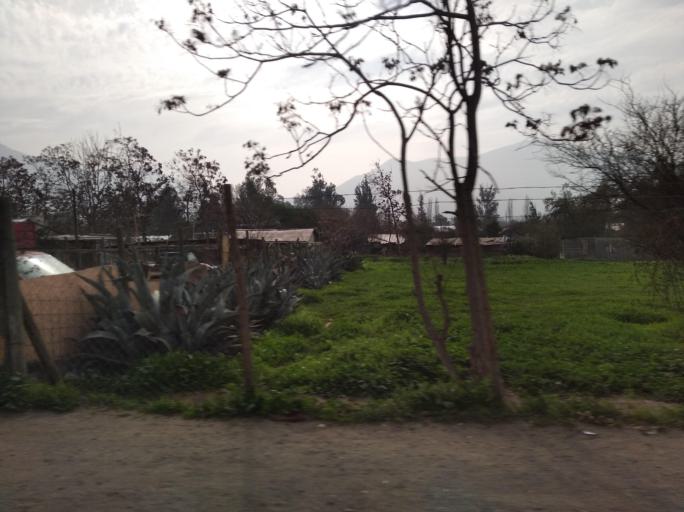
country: CL
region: Santiago Metropolitan
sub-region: Provincia de Chacabuco
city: Lampa
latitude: -33.2716
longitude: -70.8918
